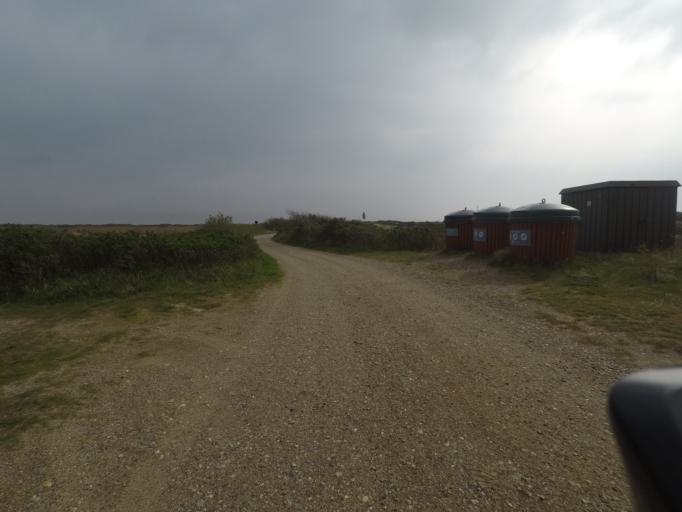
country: DE
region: Schleswig-Holstein
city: List
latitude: 55.1502
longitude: 8.4992
